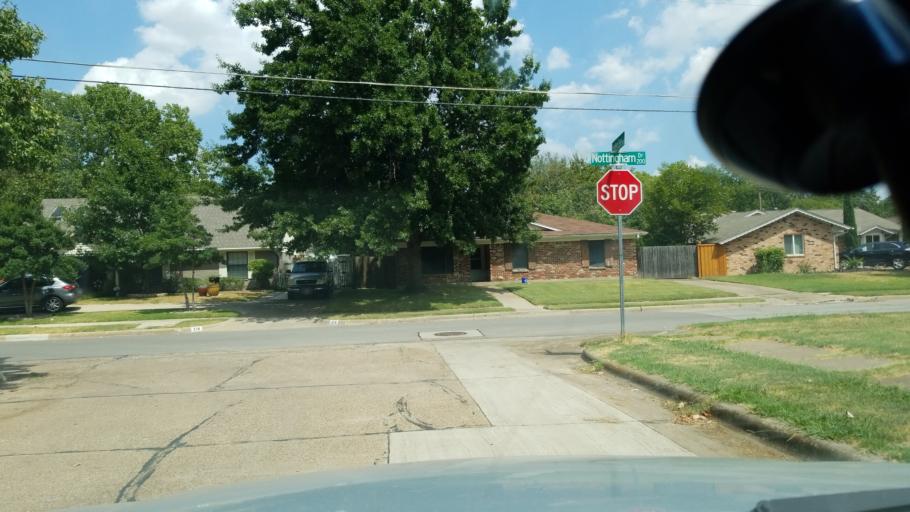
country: US
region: Texas
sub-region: Dallas County
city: Irving
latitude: 32.8177
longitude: -96.9830
